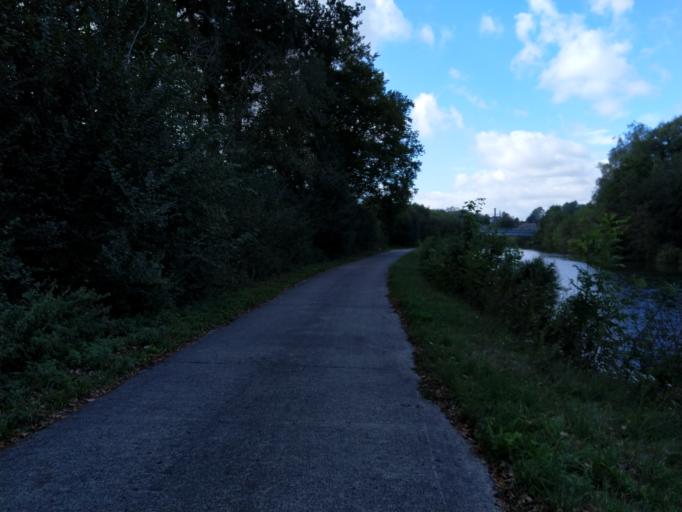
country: BE
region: Wallonia
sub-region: Province du Hainaut
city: Merbes-le-Chateau
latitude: 50.3238
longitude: 4.2181
